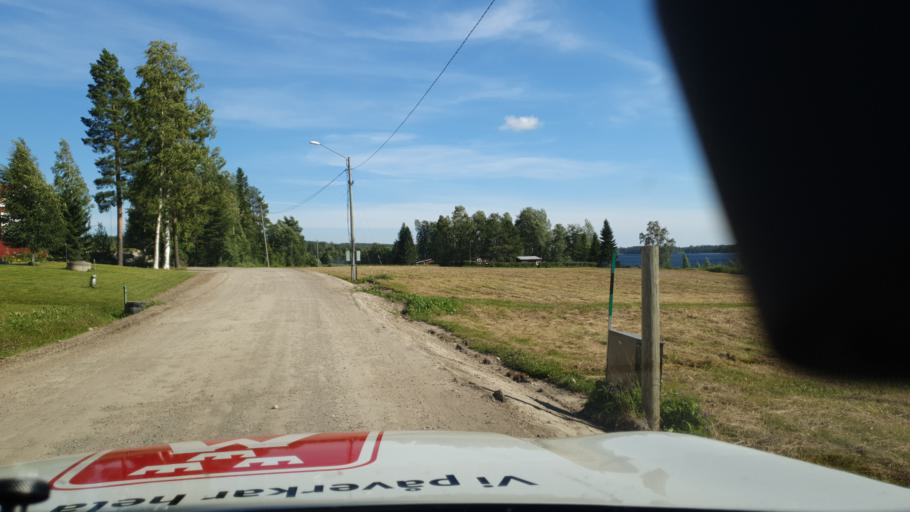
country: SE
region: Vaesterbotten
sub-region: Umea Kommun
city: Roback
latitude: 64.0019
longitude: 20.0842
